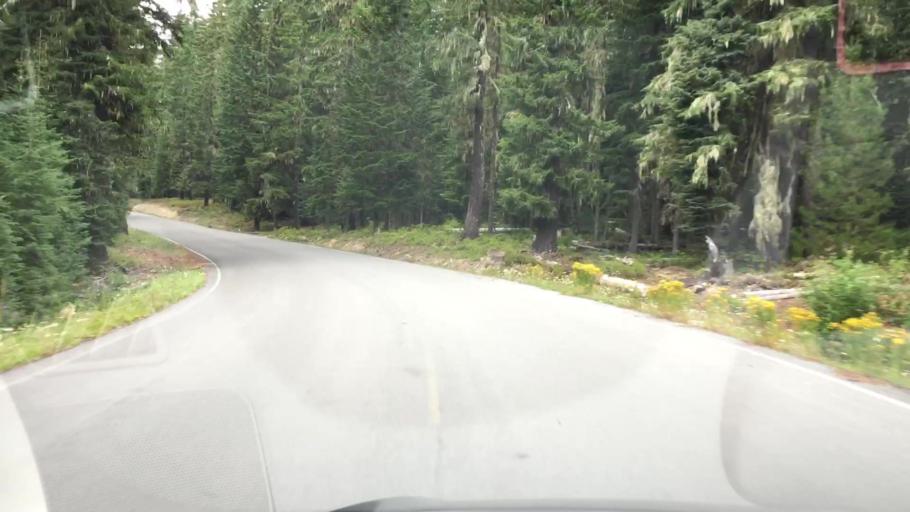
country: US
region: Washington
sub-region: Klickitat County
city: White Salmon
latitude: 46.1979
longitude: -121.6445
